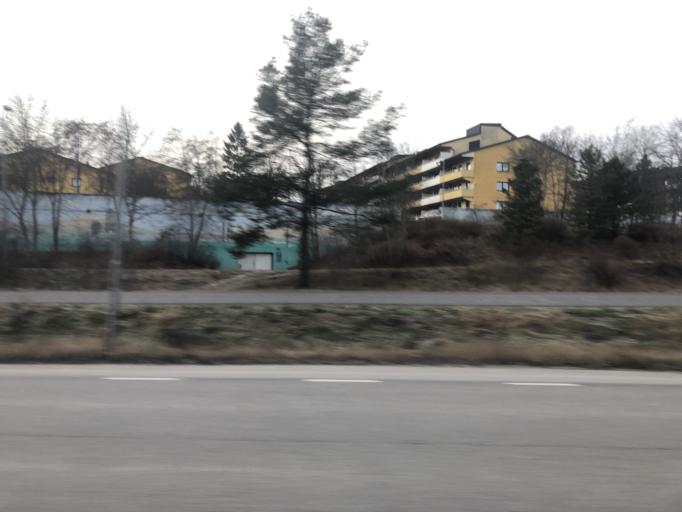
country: SE
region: Stockholm
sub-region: Jarfalla Kommun
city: Jakobsberg
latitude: 59.4145
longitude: 17.7981
